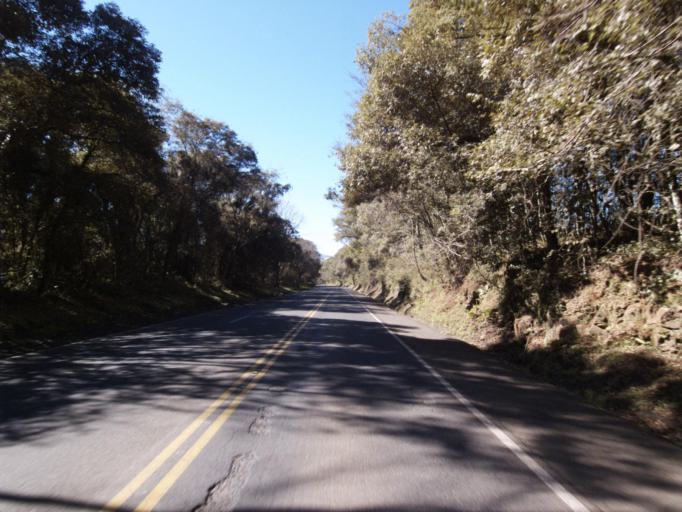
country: BR
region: Santa Catarina
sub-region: Sao Lourenco Do Oeste
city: Sao Lourenco dOeste
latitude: -26.8262
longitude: -53.0598
